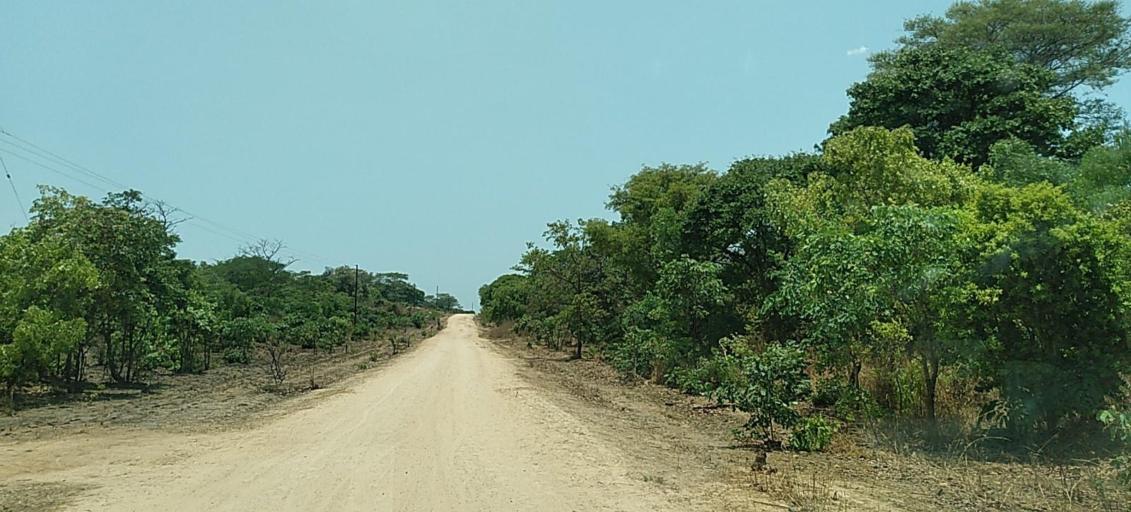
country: ZM
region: Copperbelt
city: Mpongwe
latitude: -13.8138
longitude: 27.8488
